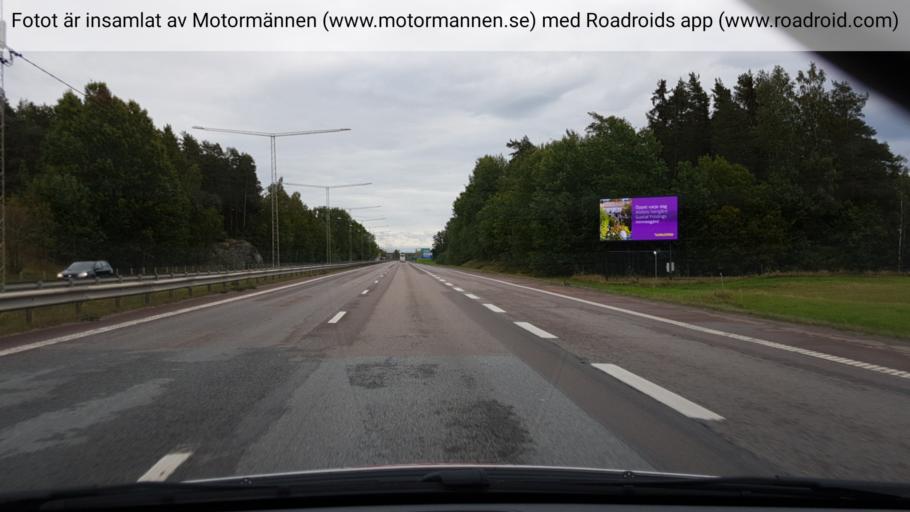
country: SE
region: Vaermland
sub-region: Karlstads Kommun
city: Karlstad
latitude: 59.3799
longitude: 13.4489
